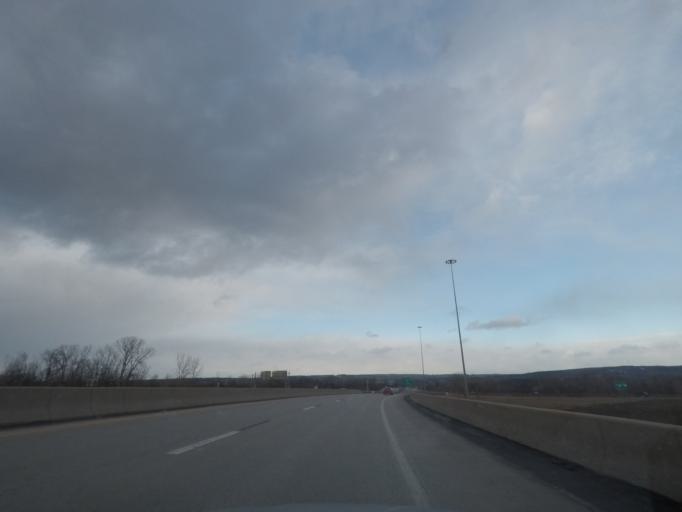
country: US
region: New York
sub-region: Oneida County
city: Utica
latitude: 43.1078
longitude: -75.2386
